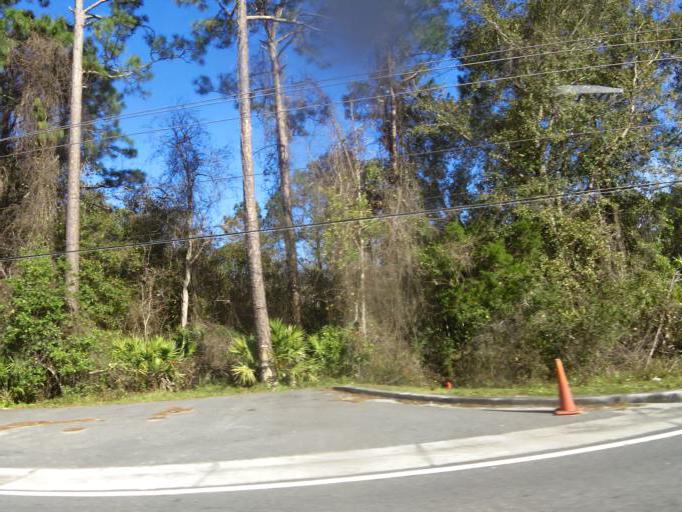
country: US
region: Florida
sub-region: Saint Johns County
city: Saint Augustine
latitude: 29.9169
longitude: -81.4031
